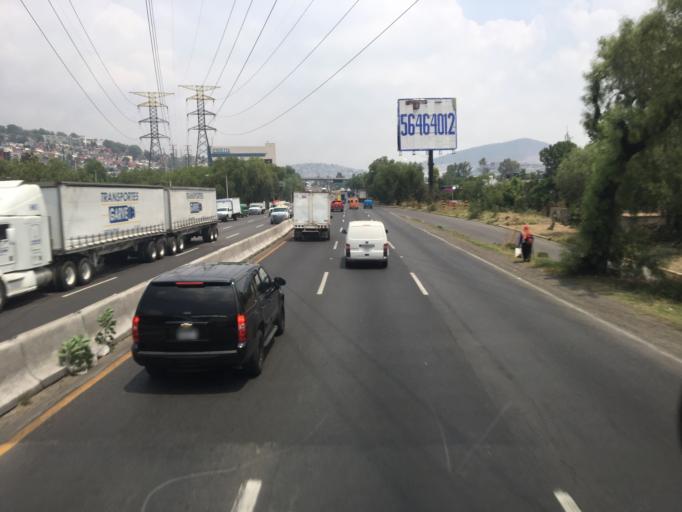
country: MX
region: Mexico
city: Tlalnepantla
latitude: 19.5650
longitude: -99.2050
